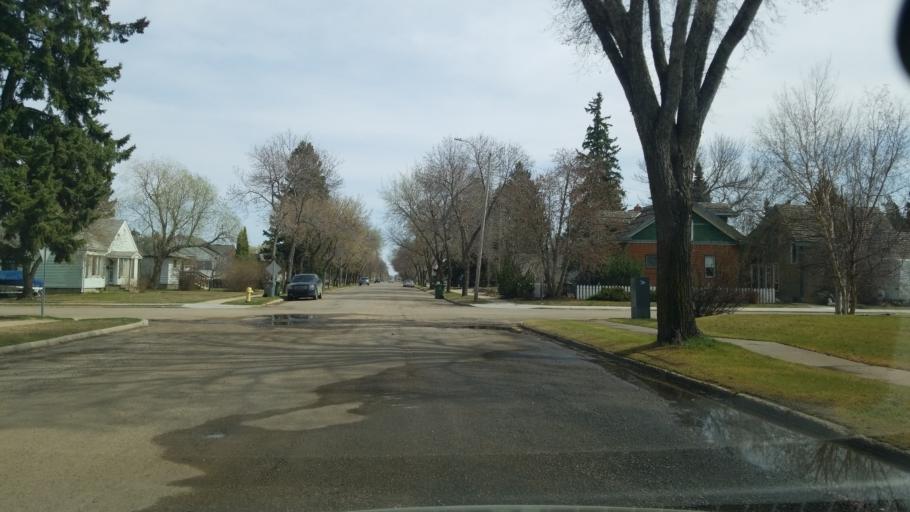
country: CA
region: Saskatchewan
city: Lloydminster
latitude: 53.2816
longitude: -110.0162
